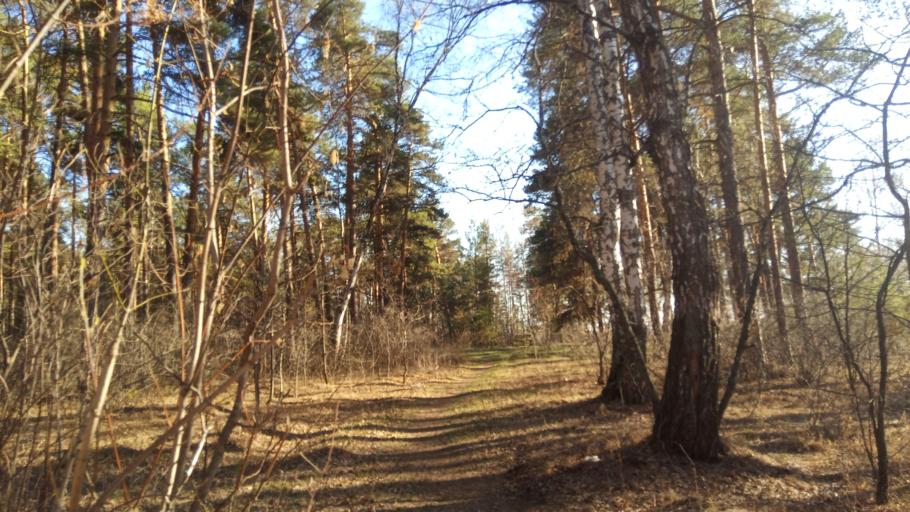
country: RU
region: Chelyabinsk
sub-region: Gorod Chelyabinsk
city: Chelyabinsk
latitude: 55.1375
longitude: 61.3287
